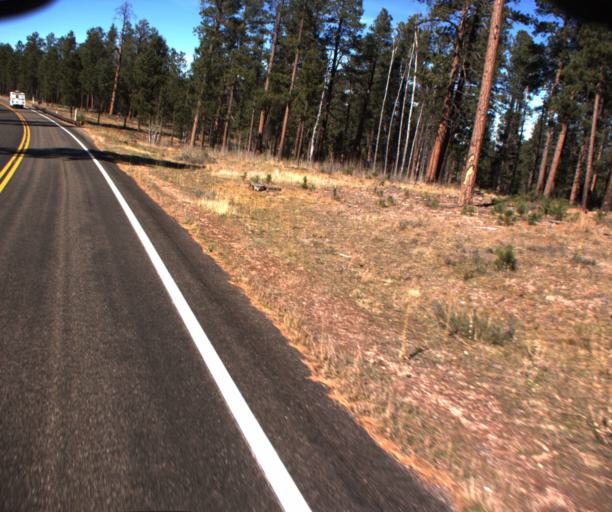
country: US
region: Arizona
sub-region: Coconino County
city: Fredonia
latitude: 36.6778
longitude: -112.2102
